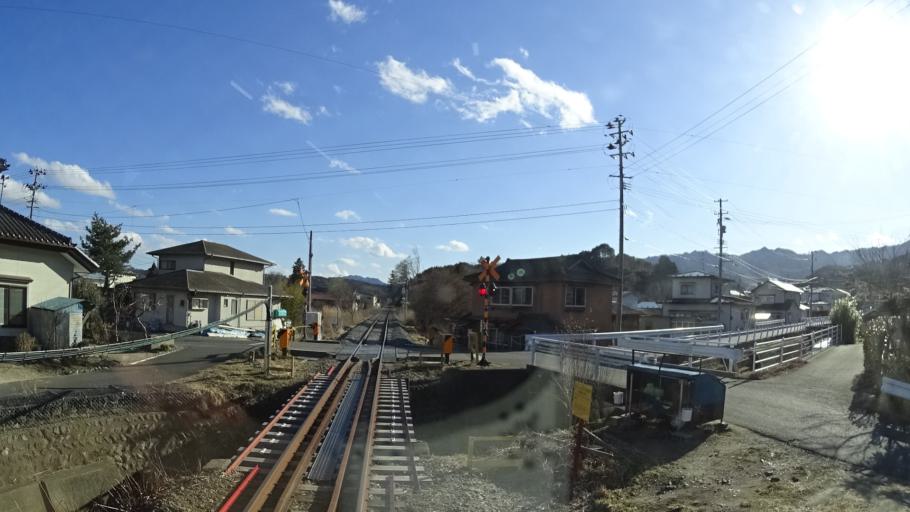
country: JP
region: Iwate
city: Miyako
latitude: 39.5768
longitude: 141.9347
